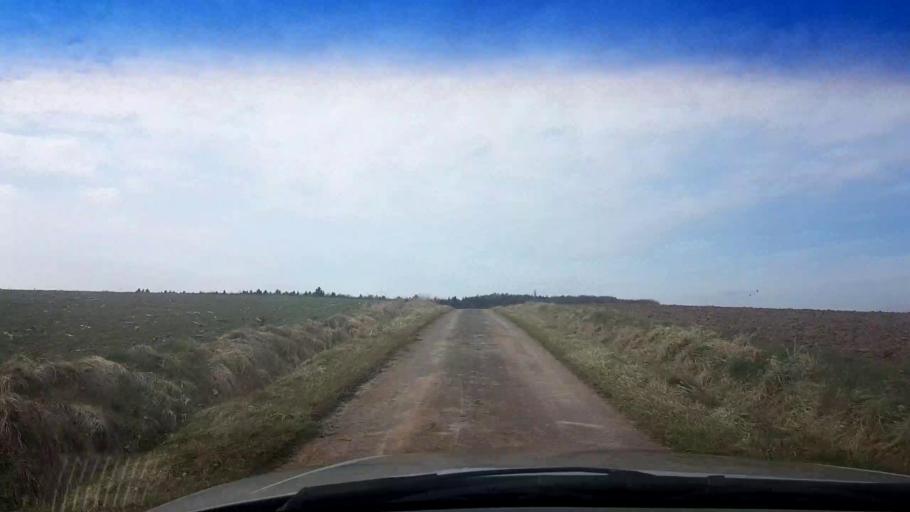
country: DE
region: Bavaria
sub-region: Upper Franconia
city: Burgebrach
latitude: 49.8012
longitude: 10.7577
